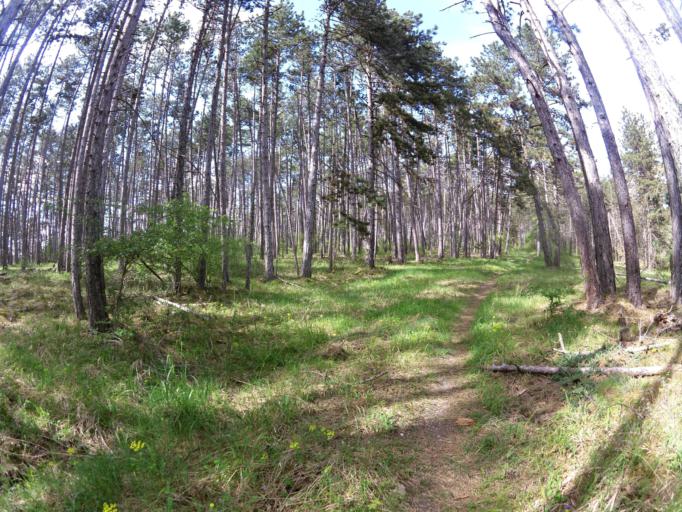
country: DE
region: Bavaria
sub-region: Regierungsbezirk Unterfranken
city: Erlabrunn
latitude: 49.8610
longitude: 9.8219
